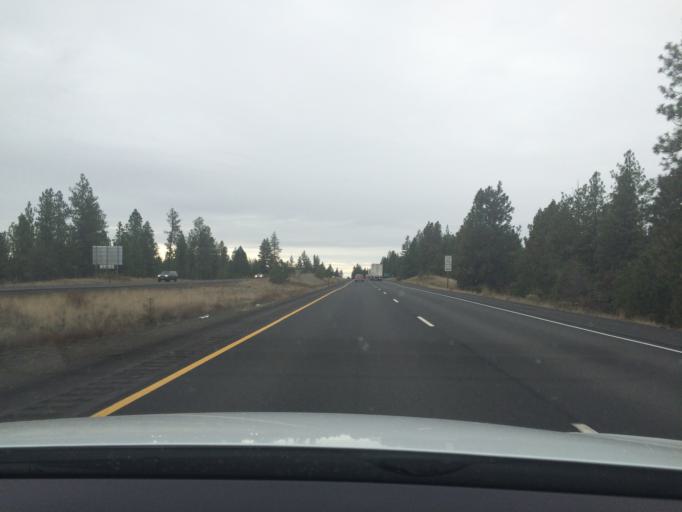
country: US
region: Washington
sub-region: Spokane County
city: Medical Lake
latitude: 47.4309
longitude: -117.7974
